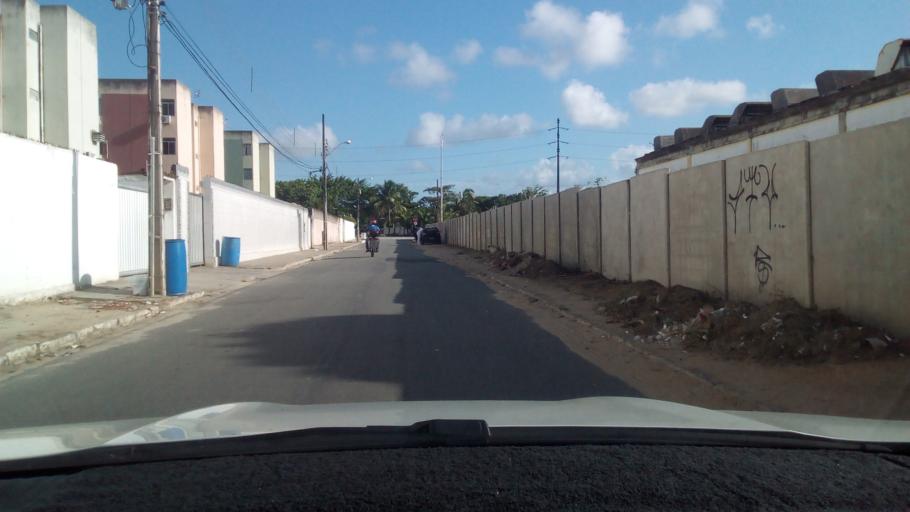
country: BR
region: Paraiba
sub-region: Joao Pessoa
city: Joao Pessoa
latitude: -7.1605
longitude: -34.8409
